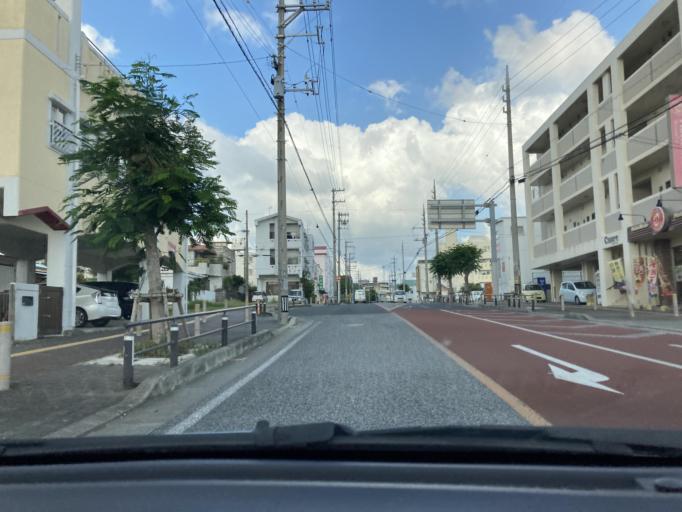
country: JP
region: Okinawa
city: Itoman
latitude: 26.1296
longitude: 127.6724
